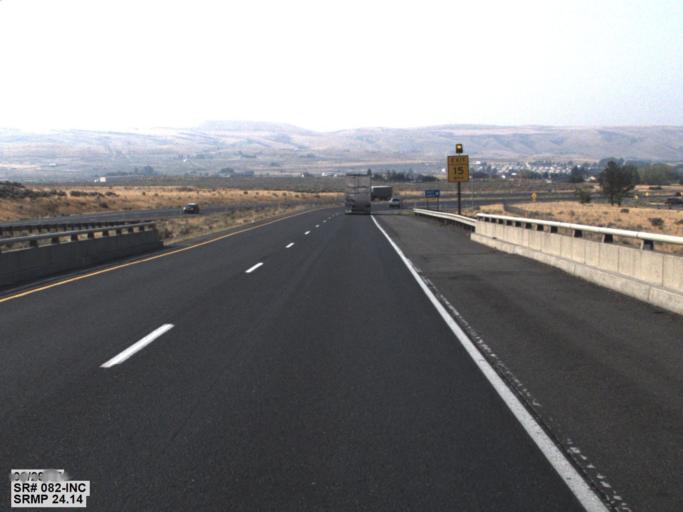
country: US
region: Washington
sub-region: Yakima County
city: Terrace Heights
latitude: 46.6991
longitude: -120.4414
